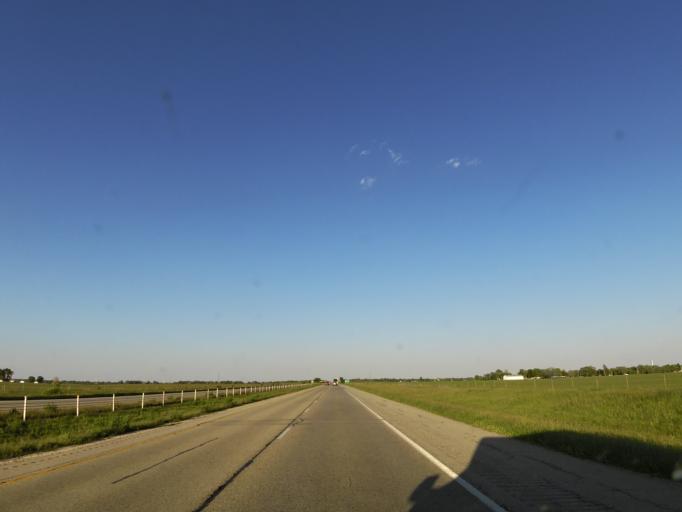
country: US
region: Illinois
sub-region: Vermilion County
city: Oakwood
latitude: 40.1239
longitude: -87.8884
